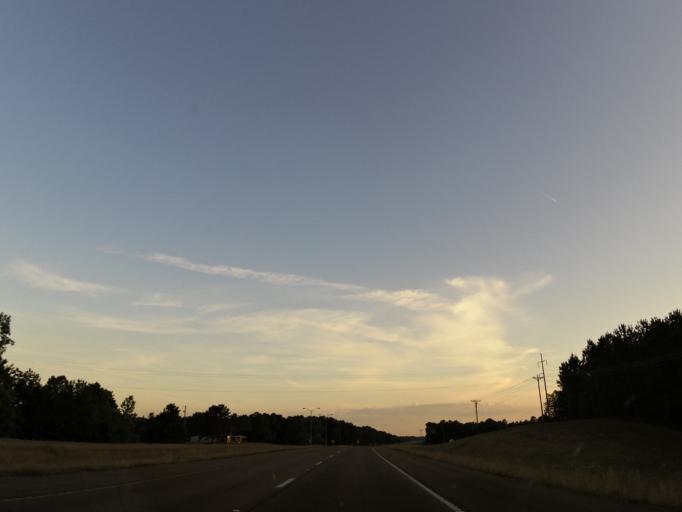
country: US
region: Mississippi
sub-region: Noxubee County
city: Macon
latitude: 33.0933
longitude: -88.5486
